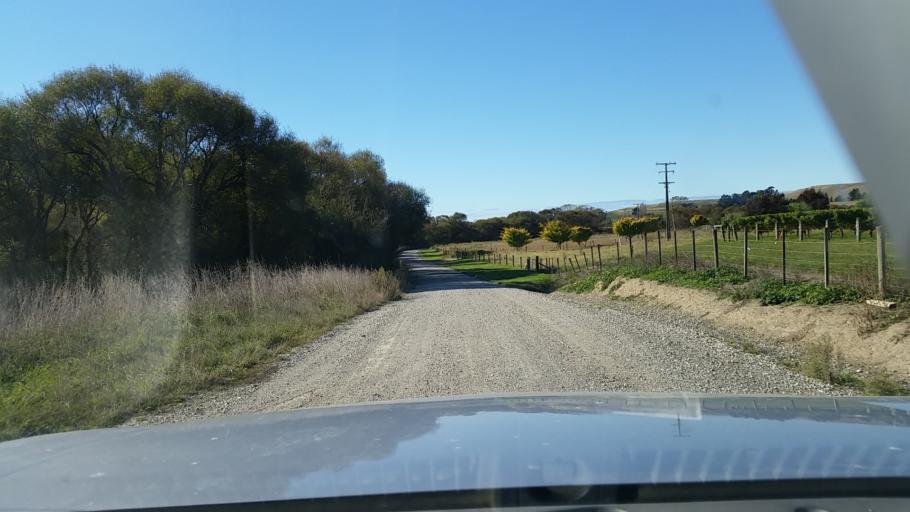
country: NZ
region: Marlborough
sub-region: Marlborough District
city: Blenheim
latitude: -41.6800
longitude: 174.1346
